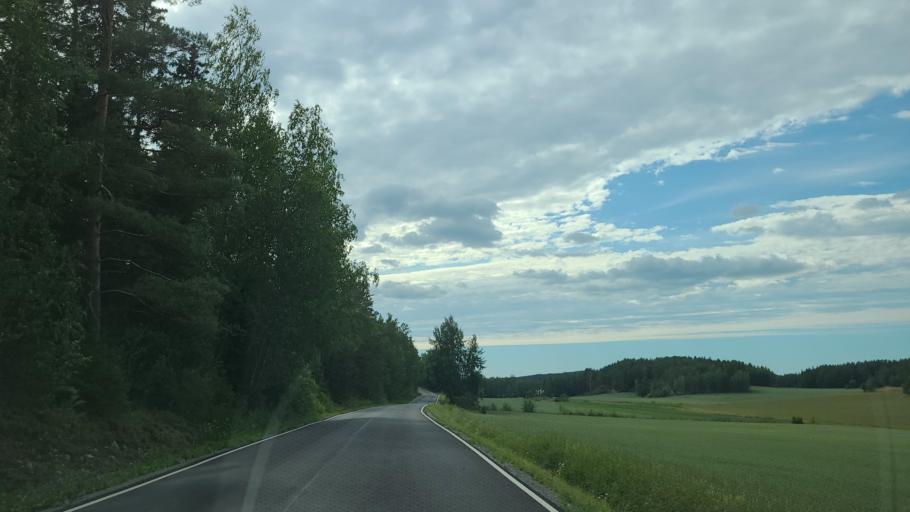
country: FI
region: Varsinais-Suomi
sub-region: Turku
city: Rymaettylae
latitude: 60.3257
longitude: 21.9650
